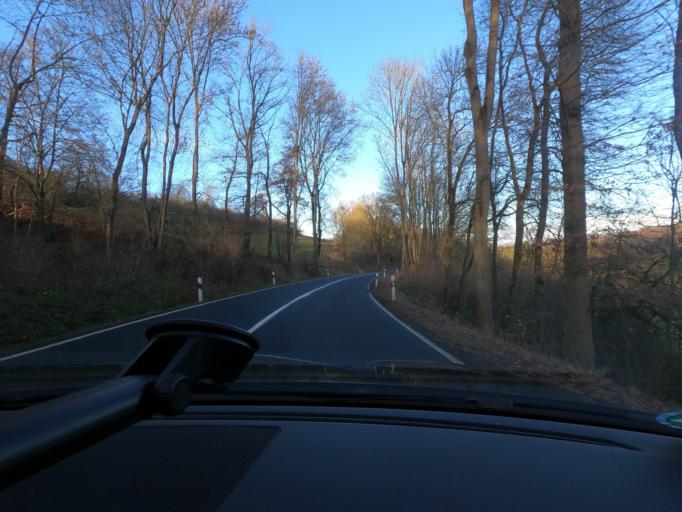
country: DE
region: Lower Saxony
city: Rhumspringe
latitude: 51.5470
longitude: 10.3008
